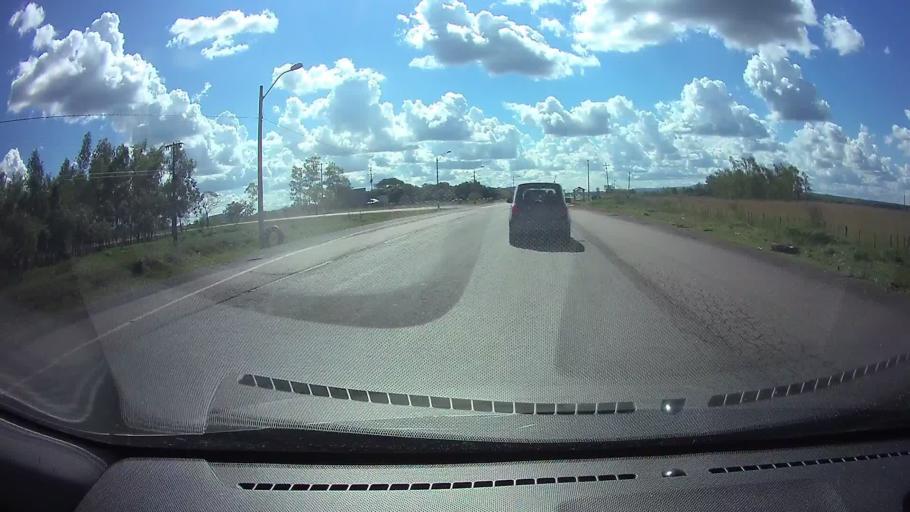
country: PY
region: Paraguari
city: La Colmena
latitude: -25.7477
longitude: -56.8007
